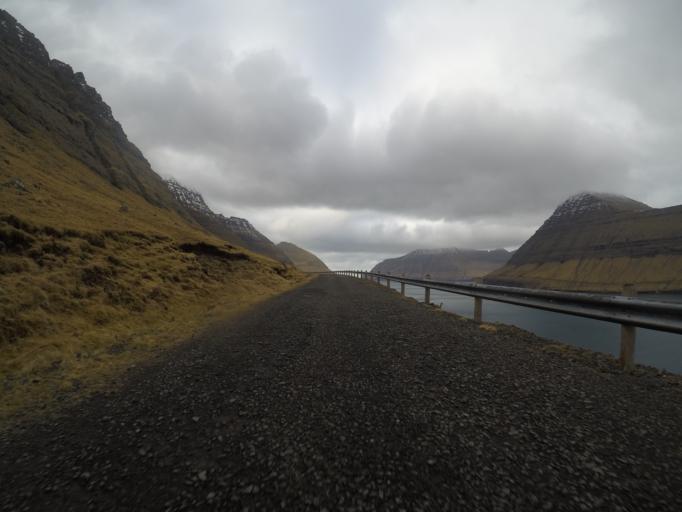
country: FO
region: Nordoyar
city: Klaksvik
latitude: 62.3232
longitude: -6.5618
